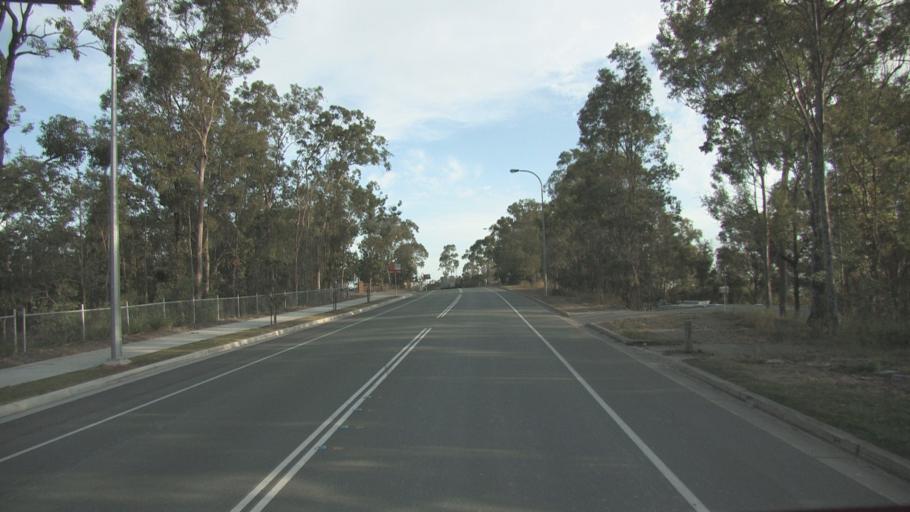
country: AU
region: Queensland
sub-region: Logan
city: Waterford West
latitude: -27.7158
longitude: 153.1584
